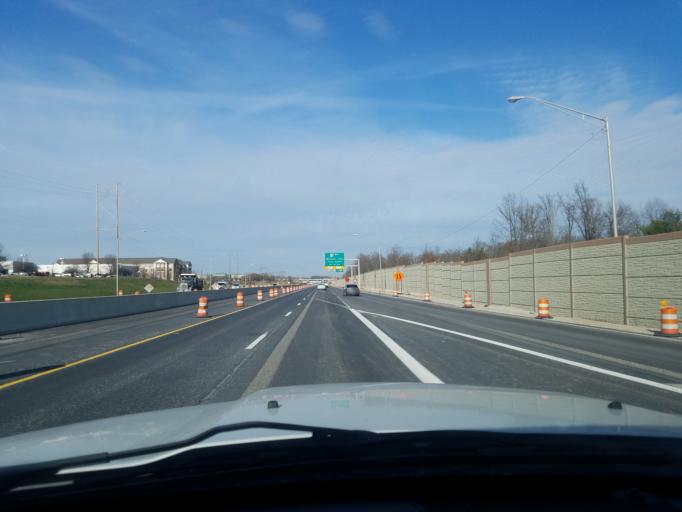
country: US
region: Indiana
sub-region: Monroe County
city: Bloomington
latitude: 39.1524
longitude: -86.5729
